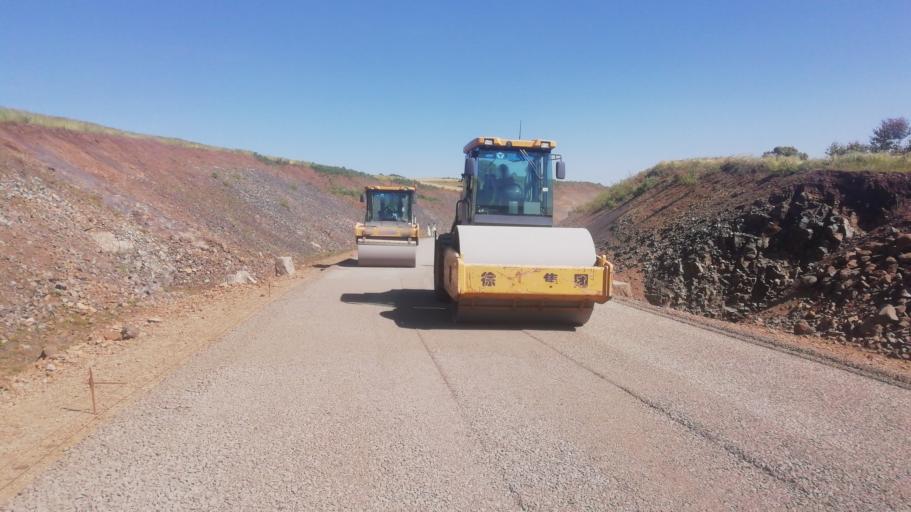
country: ET
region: Amhara
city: Addiet Canna
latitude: 11.3651
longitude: 37.8709
